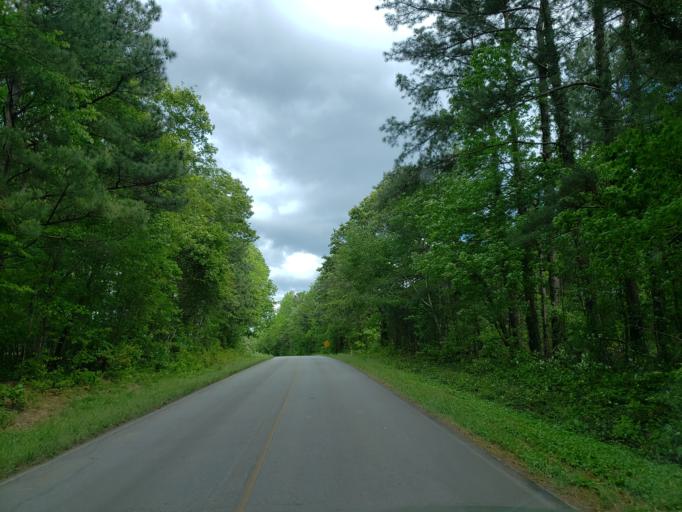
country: US
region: Georgia
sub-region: Haralson County
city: Tallapoosa
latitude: 33.6849
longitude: -85.3183
